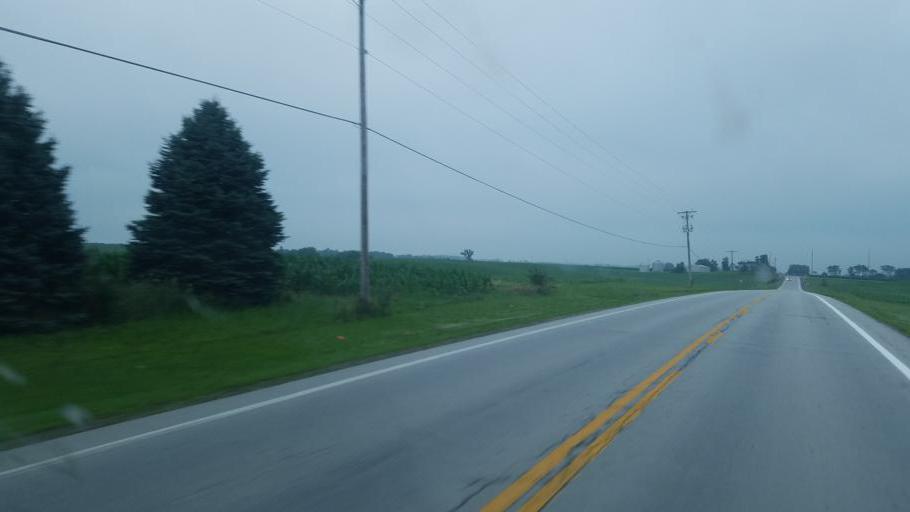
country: US
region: Ohio
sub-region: Fayette County
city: Washington Court House
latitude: 39.5954
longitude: -83.3833
